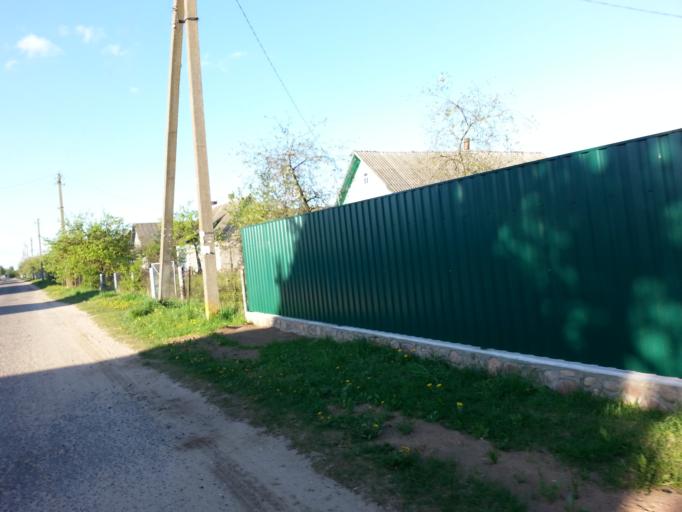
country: BY
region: Minsk
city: Narach
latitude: 54.9333
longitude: 26.6904
